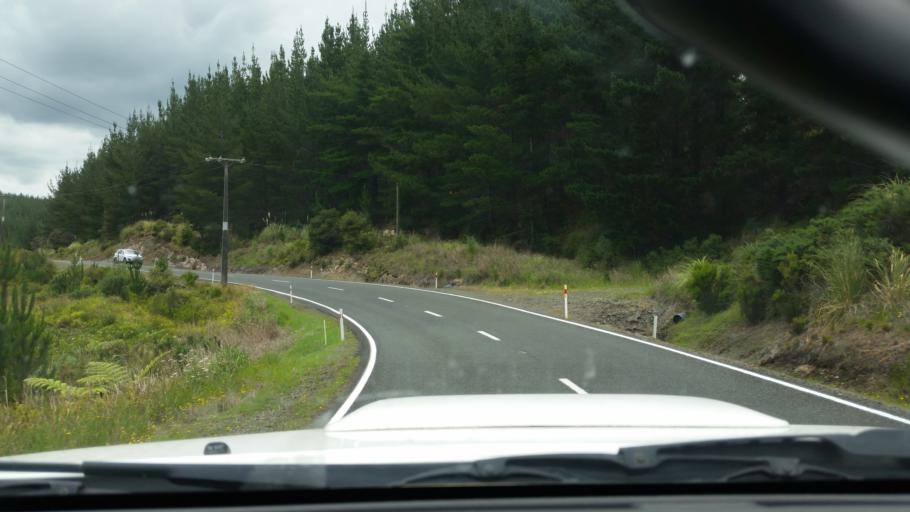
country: NZ
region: Northland
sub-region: Kaipara District
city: Dargaville
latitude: -35.8164
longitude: 173.7172
